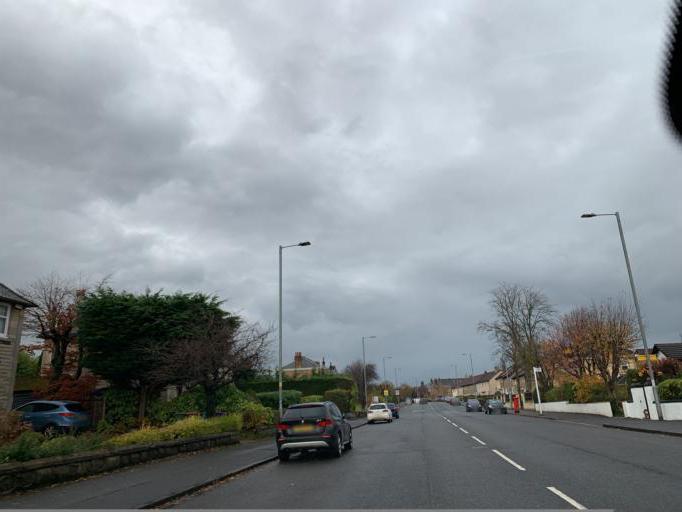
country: GB
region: Scotland
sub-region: East Renfrewshire
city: Giffnock
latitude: 55.8142
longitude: -4.2712
